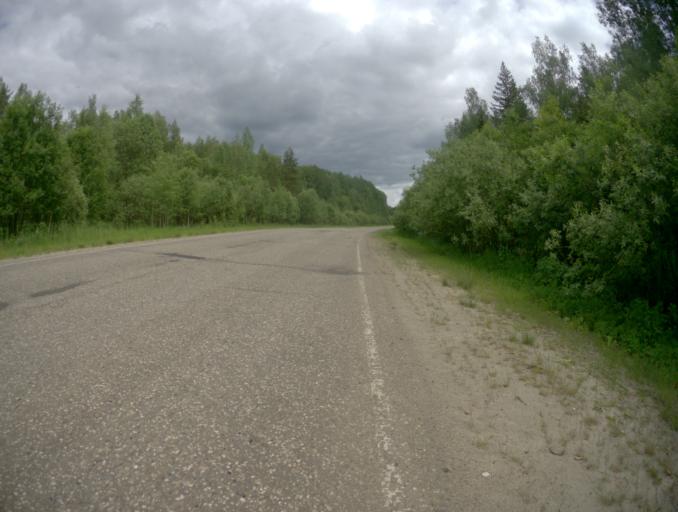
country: RU
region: Ivanovo
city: Arkhipovka
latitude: 56.6209
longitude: 41.2820
